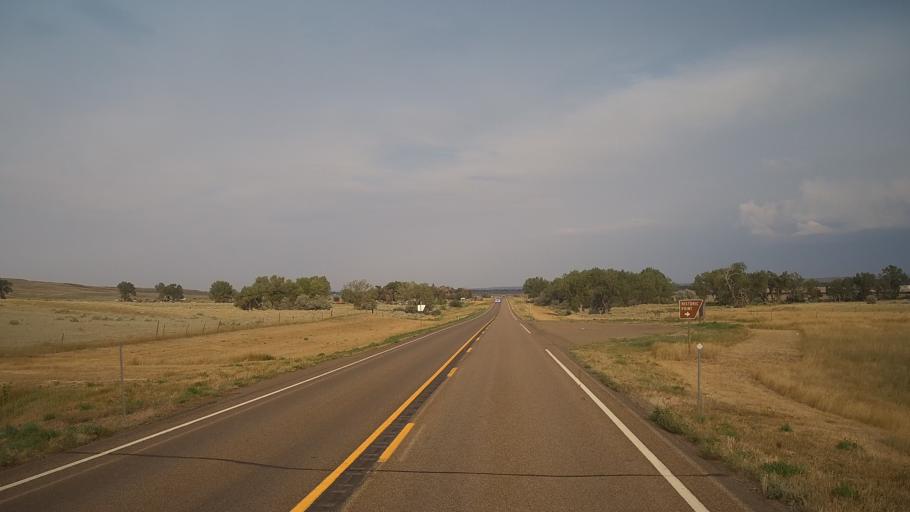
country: US
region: Montana
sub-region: Phillips County
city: Malta
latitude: 48.3693
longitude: -107.9664
